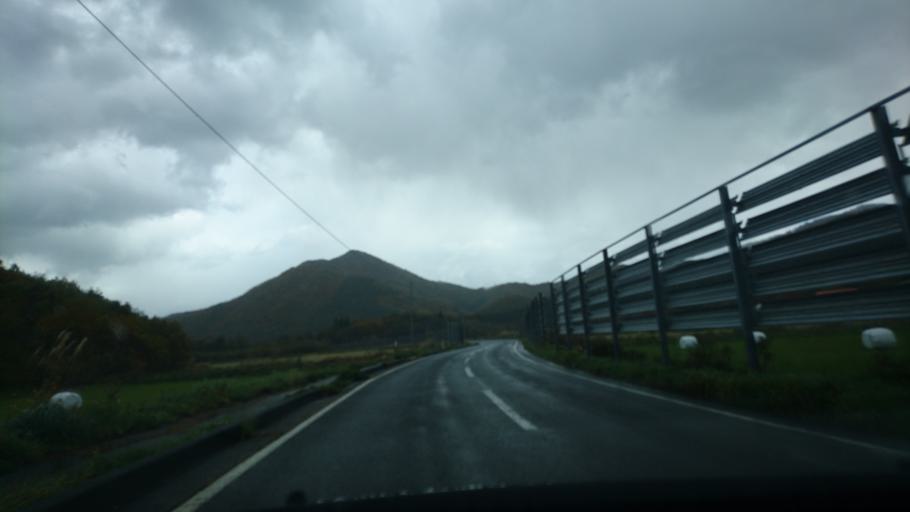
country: JP
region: Iwate
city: Shizukuishi
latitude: 39.6079
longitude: 140.9331
